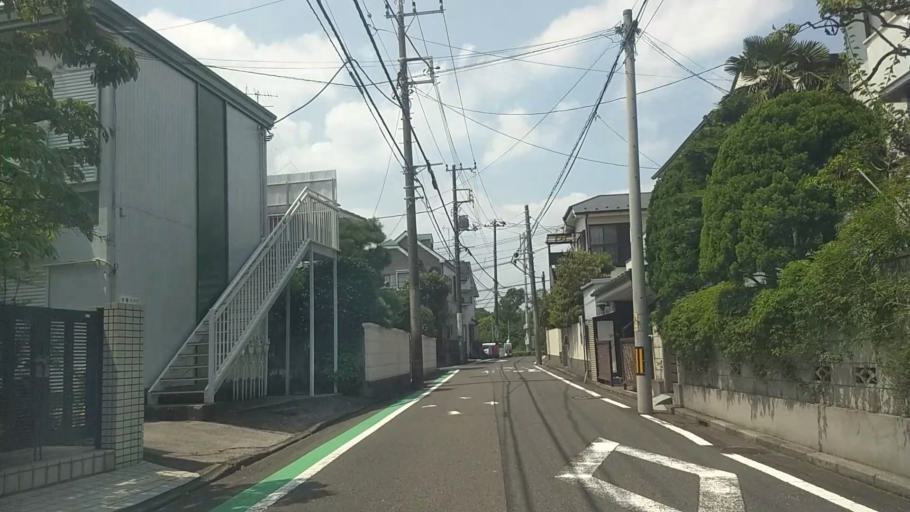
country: JP
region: Kanagawa
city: Yokohama
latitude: 35.4922
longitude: 139.6149
